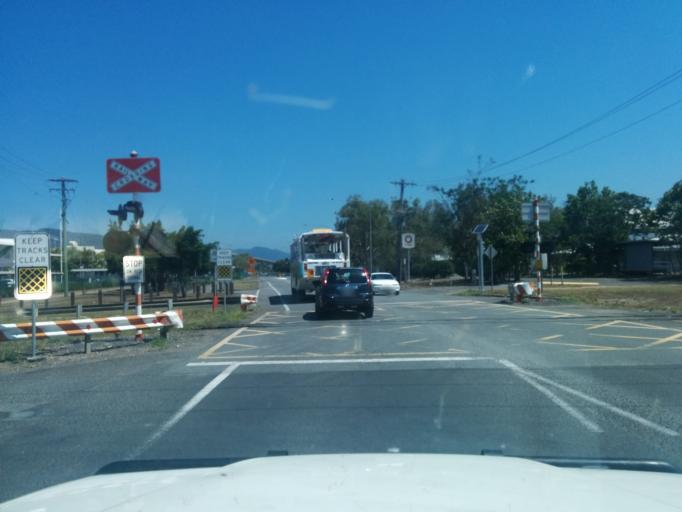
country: AU
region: Queensland
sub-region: Cairns
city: Cairns
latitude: -16.9355
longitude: 145.7762
